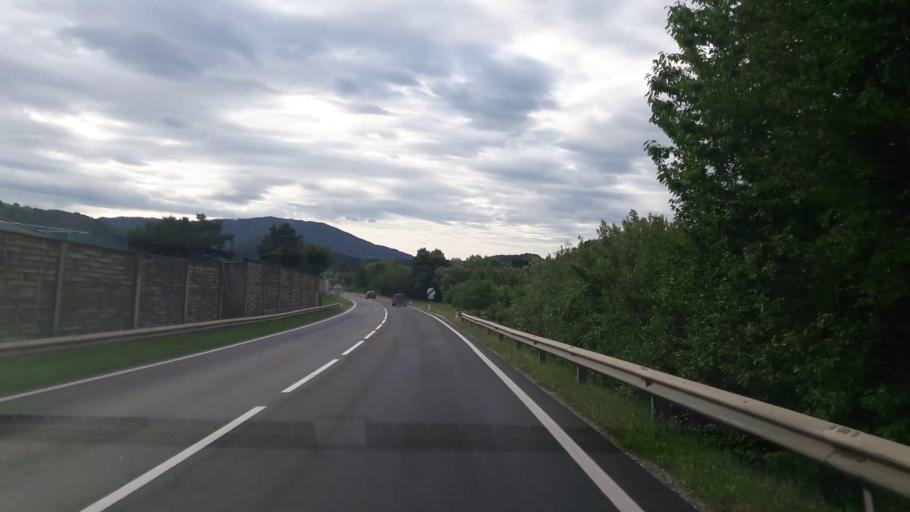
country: AT
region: Styria
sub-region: Politischer Bezirk Weiz
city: Anger
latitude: 47.2706
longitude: 15.6954
